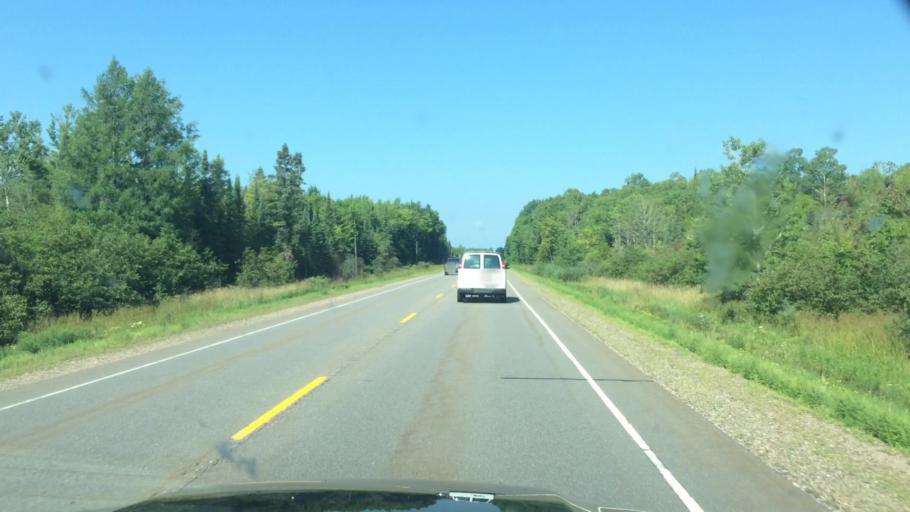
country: US
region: Wisconsin
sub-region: Lincoln County
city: Merrill
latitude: 45.1484
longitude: -89.4489
